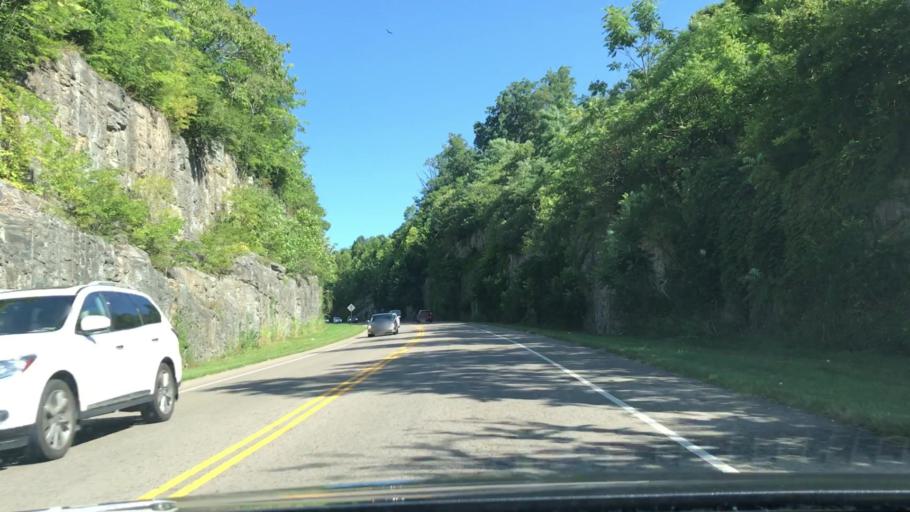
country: US
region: Tennessee
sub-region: Williamson County
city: Franklin
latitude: 35.9775
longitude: -86.8405
